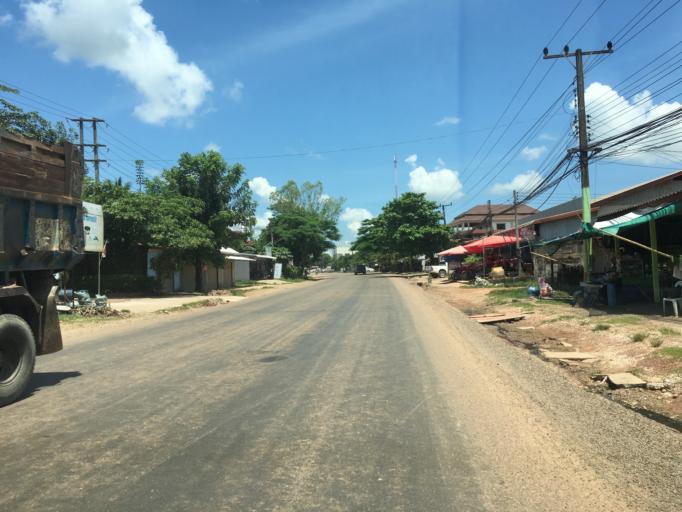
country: LA
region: Vientiane
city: Vientiane
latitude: 18.0633
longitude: 102.5383
